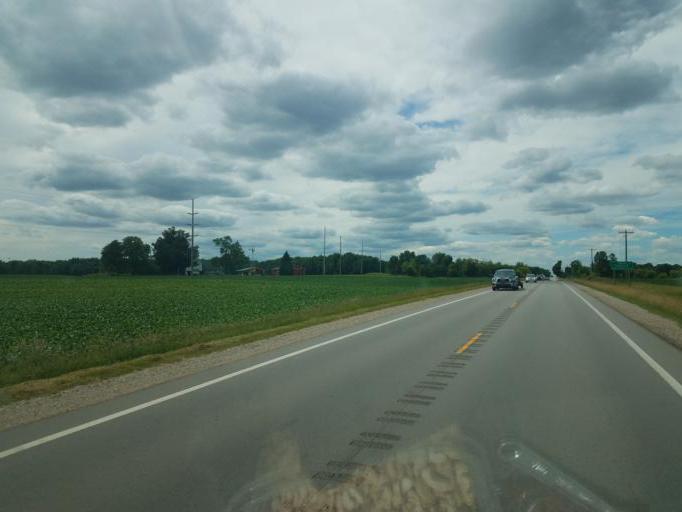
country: US
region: Michigan
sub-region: Eaton County
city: Charlotte
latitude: 42.6463
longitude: -84.8931
